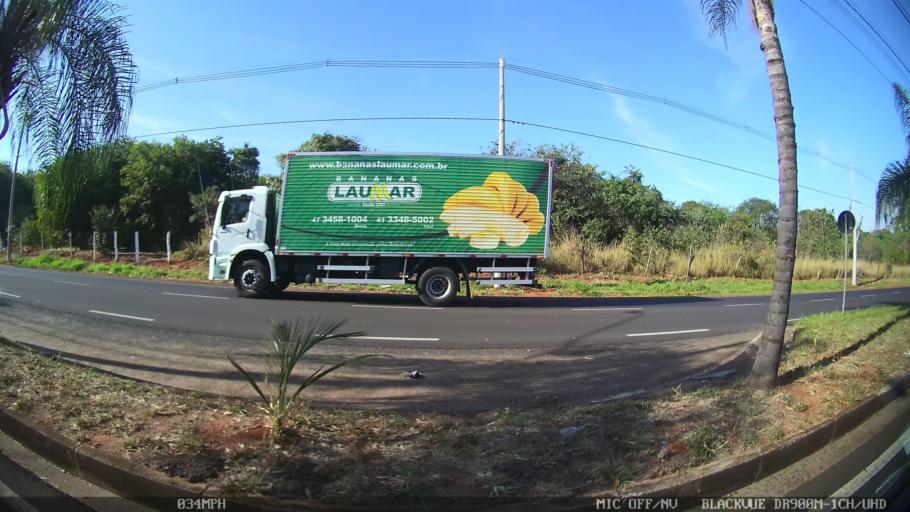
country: BR
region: Sao Paulo
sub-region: Sao Jose Do Rio Preto
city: Sao Jose do Rio Preto
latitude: -20.7666
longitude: -49.3544
